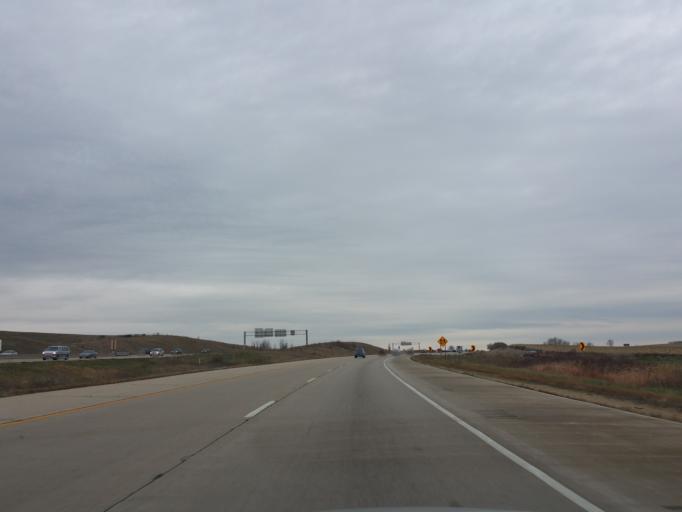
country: US
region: Wisconsin
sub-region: Columbia County
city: Portage
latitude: 43.4838
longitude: -89.4925
